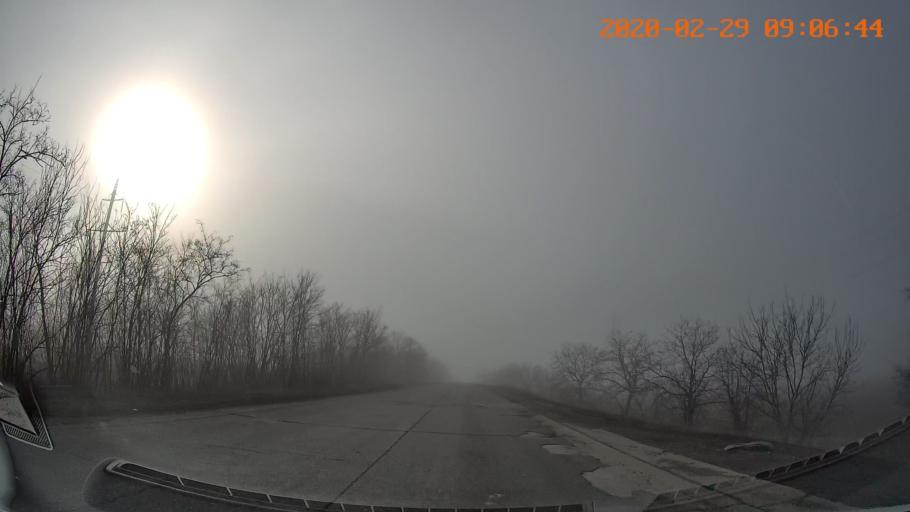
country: MD
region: Telenesti
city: Tiraspolul Nou
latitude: 46.8716
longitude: 29.7459
